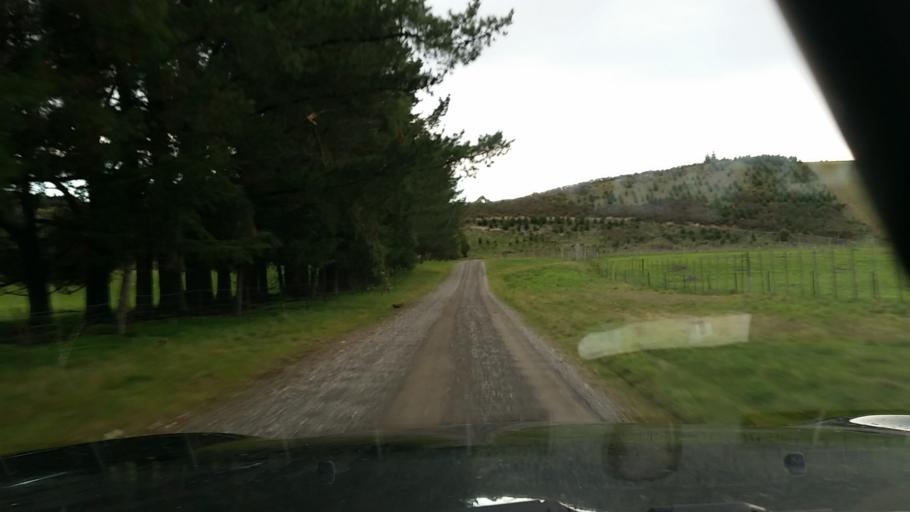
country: NZ
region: Marlborough
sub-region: Marlborough District
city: Blenheim
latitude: -41.5420
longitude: 173.6067
